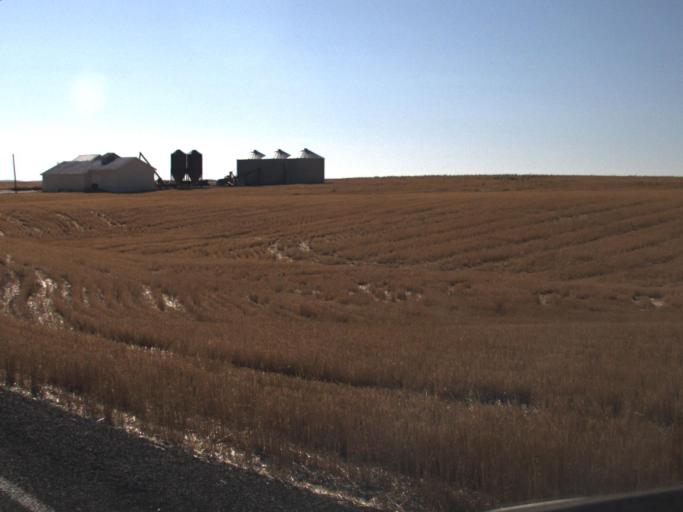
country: US
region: Washington
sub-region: Adams County
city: Ritzville
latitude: 46.8465
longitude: -118.5466
